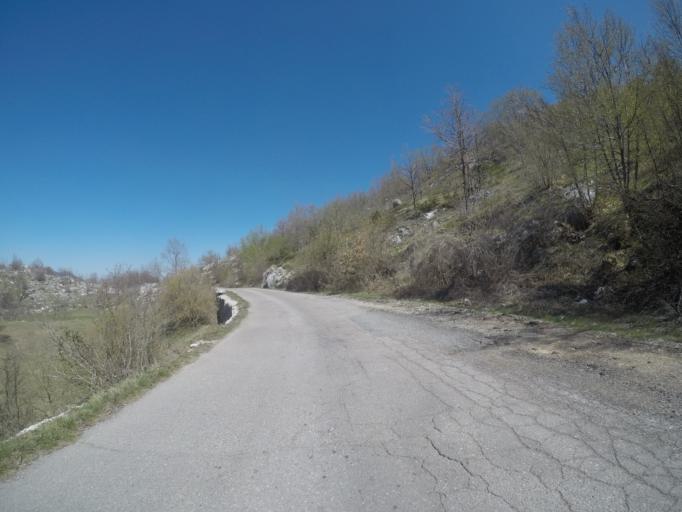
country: ME
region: Cetinje
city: Cetinje
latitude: 42.4432
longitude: 18.8742
